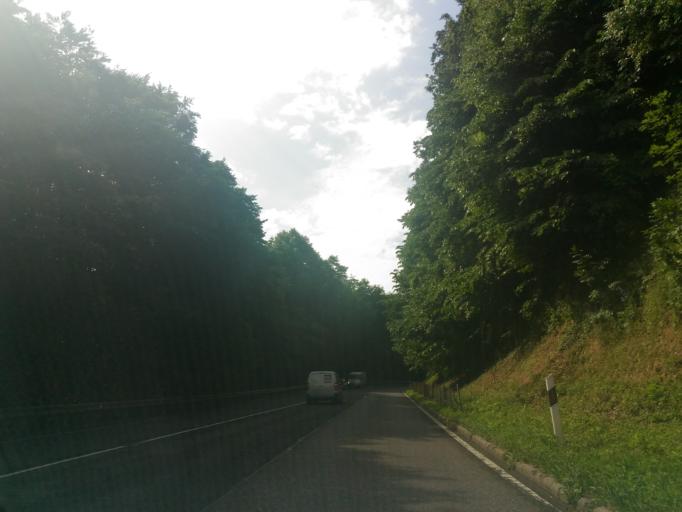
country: HU
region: Baranya
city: Komlo
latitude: 46.1503
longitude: 18.2434
